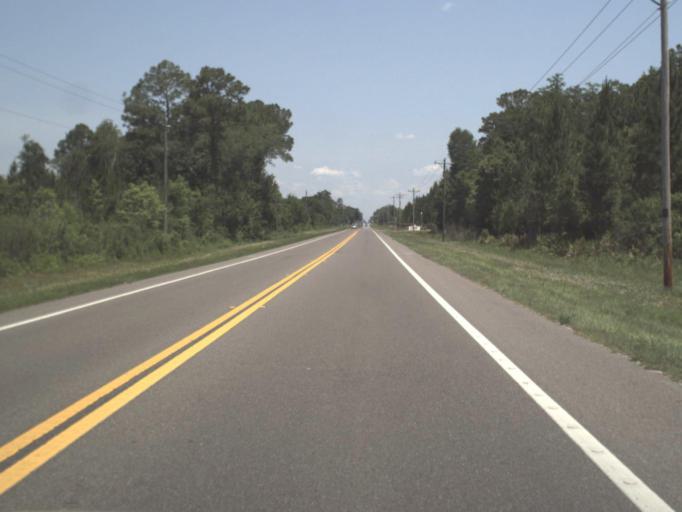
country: US
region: Florida
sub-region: Clay County
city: Keystone Heights
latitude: 29.8287
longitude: -82.0610
